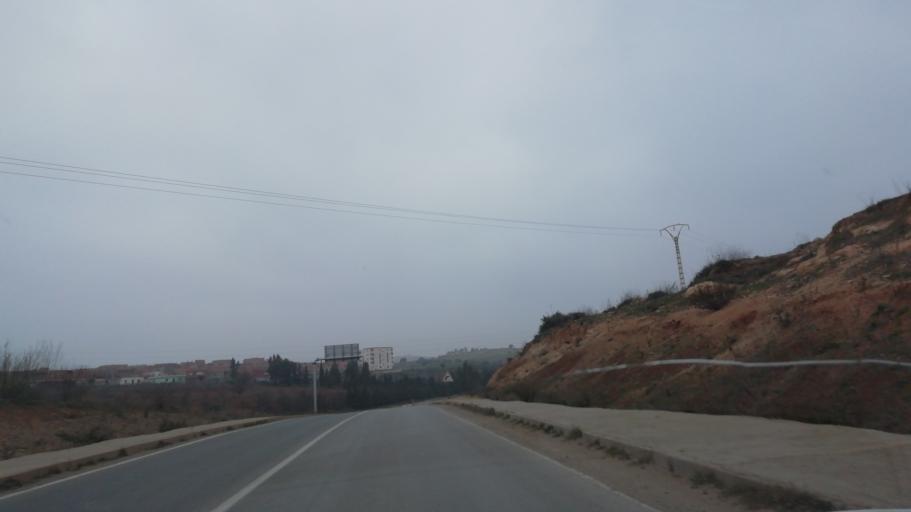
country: DZ
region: Mascara
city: Mascara
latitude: 35.4153
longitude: 0.1213
